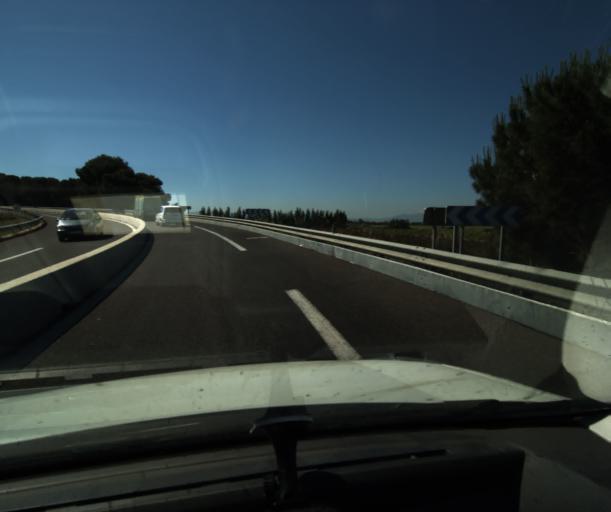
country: FR
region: Languedoc-Roussillon
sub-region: Departement des Pyrenees-Orientales
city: Rivesaltes
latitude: 42.7838
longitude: 2.8935
